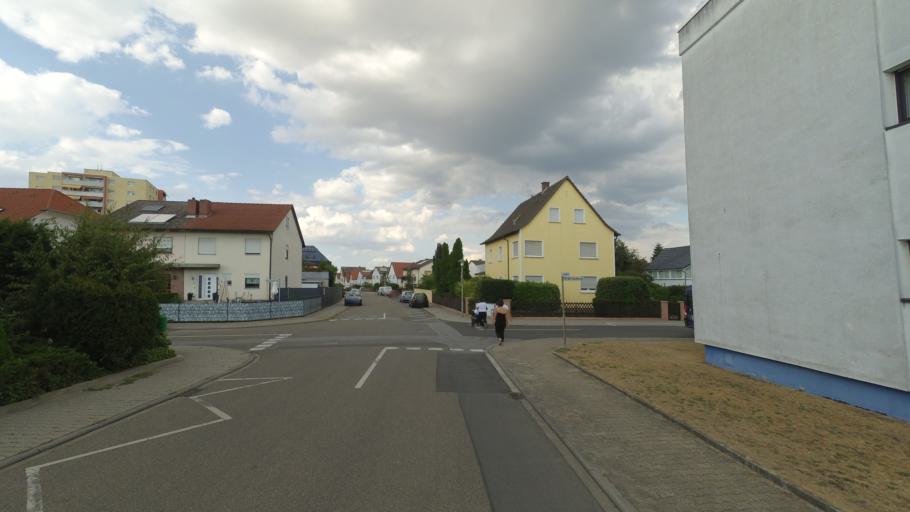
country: DE
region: Hesse
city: Lampertheim
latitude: 49.5978
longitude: 8.4590
